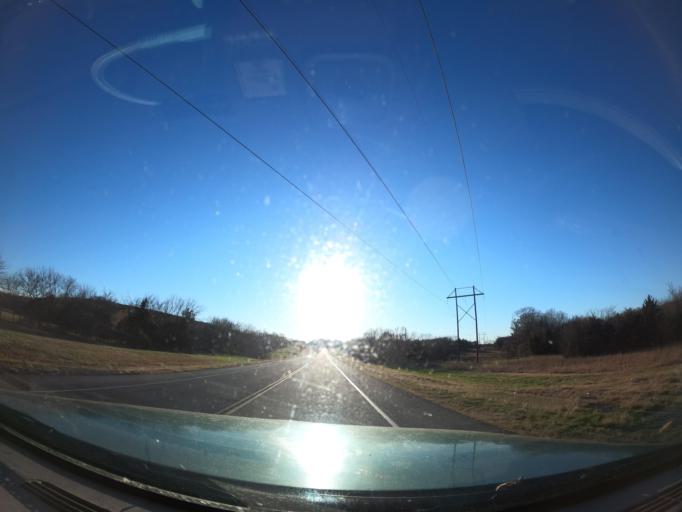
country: US
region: Oklahoma
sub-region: Pittsburg County
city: Hartshorne
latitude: 34.8681
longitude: -95.5200
